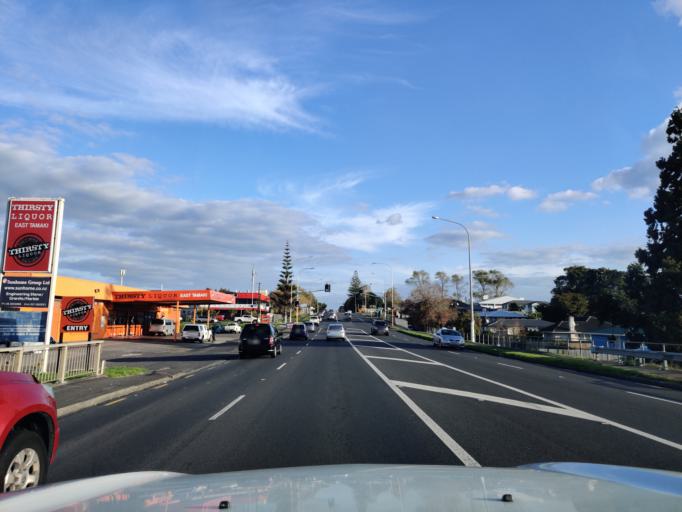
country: NZ
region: Auckland
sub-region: Auckland
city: Manukau City
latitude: -36.9555
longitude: 174.8904
